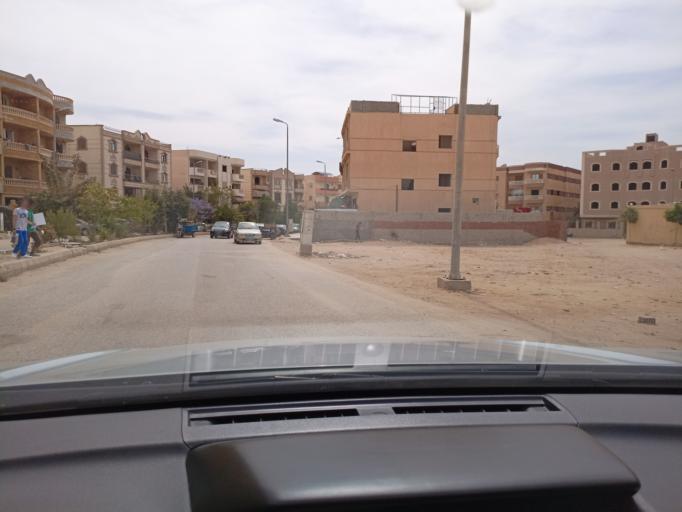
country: EG
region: Muhafazat al Qalyubiyah
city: Al Khankah
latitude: 30.2409
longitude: 31.4837
